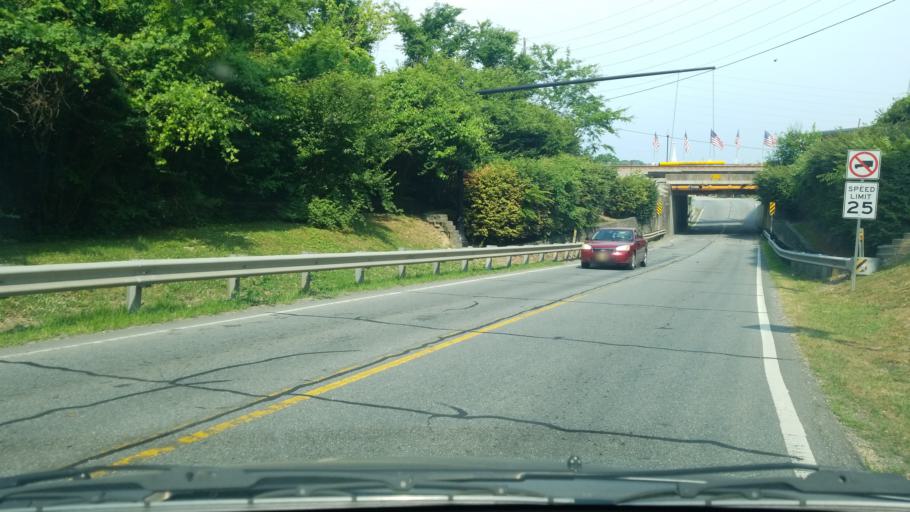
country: US
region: Georgia
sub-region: Catoosa County
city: Ringgold
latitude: 34.9145
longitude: -85.1067
